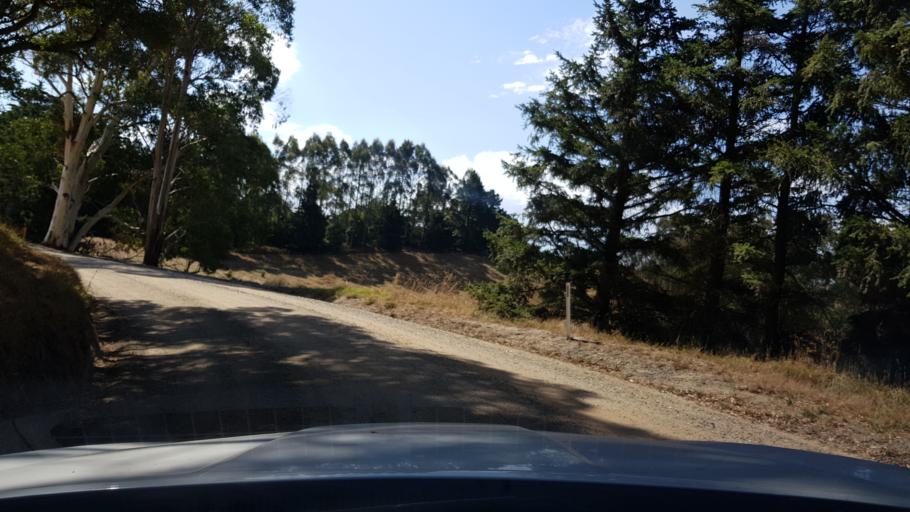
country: AU
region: Victoria
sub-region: Baw Baw
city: Warragul
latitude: -38.2982
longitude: 145.9128
